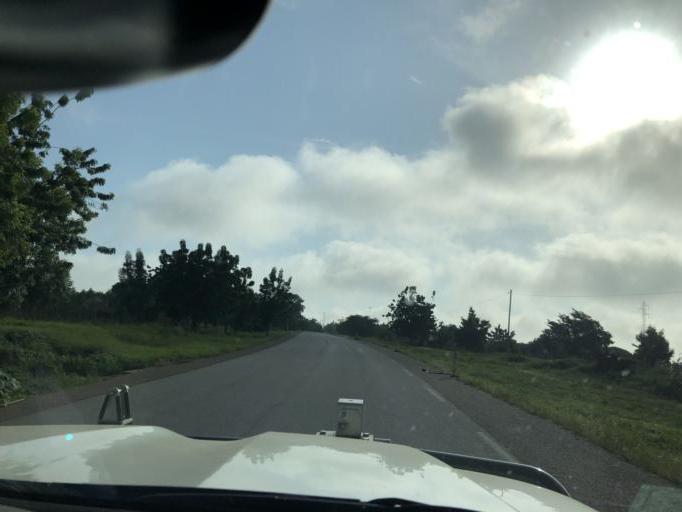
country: CM
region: North Province
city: Pitoa
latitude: 9.4937
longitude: 13.6871
